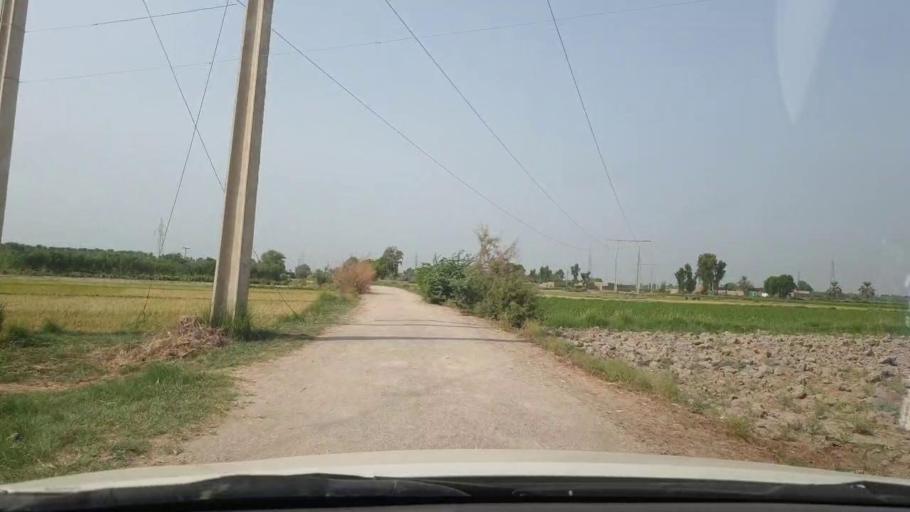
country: PK
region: Sindh
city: Shikarpur
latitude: 27.9783
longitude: 68.6742
